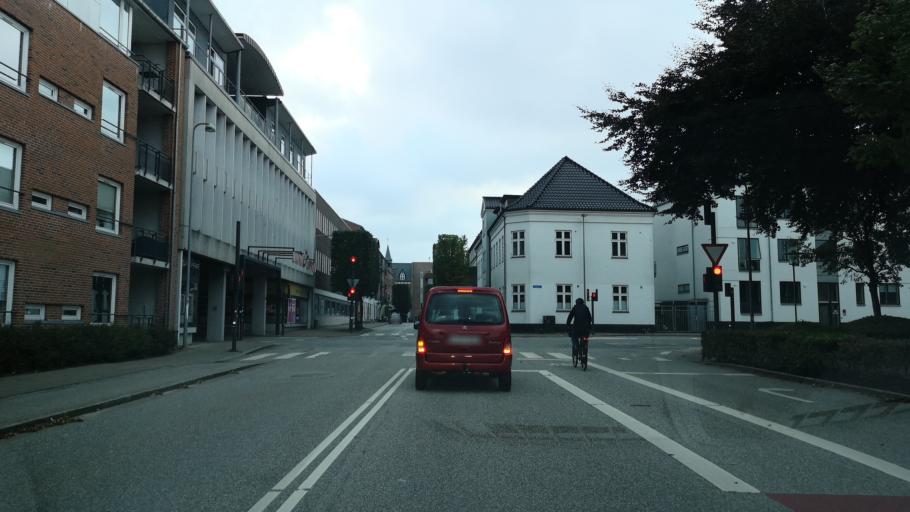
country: DK
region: Central Jutland
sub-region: Herning Kommune
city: Herning
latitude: 56.1376
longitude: 8.9782
